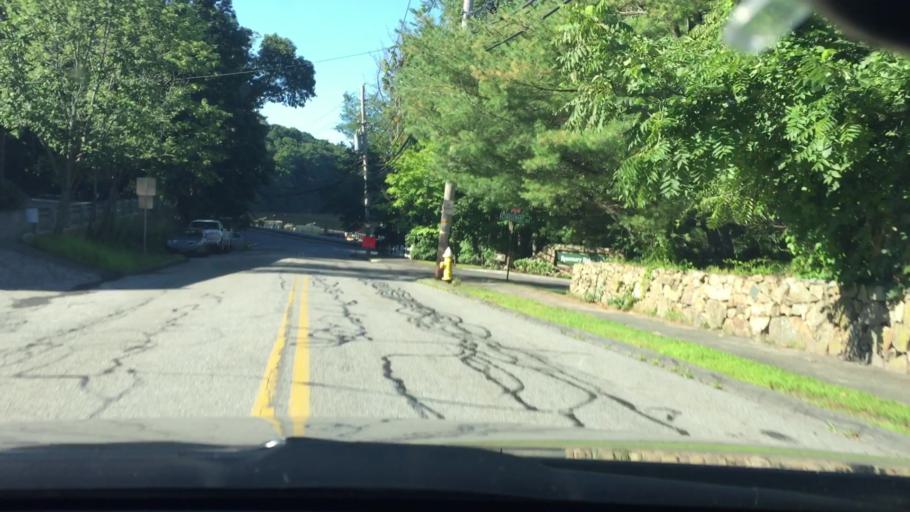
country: US
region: Massachusetts
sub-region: Norfolk County
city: Needham
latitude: 42.2895
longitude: -71.2380
